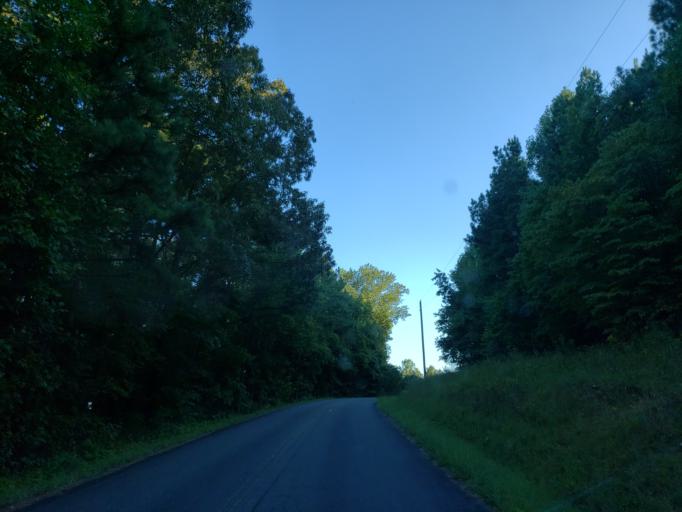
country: US
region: Georgia
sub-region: Bartow County
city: Rydal
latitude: 34.3997
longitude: -84.6719
